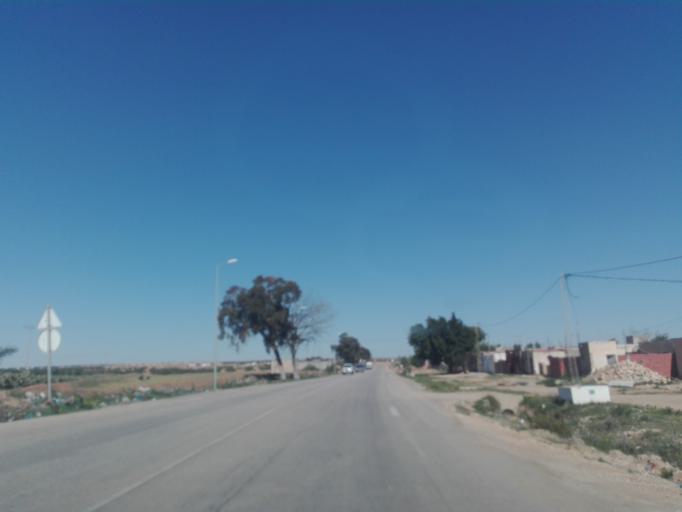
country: TN
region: Safaqis
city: Bi'r `Ali Bin Khalifah
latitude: 34.7416
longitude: 10.3697
